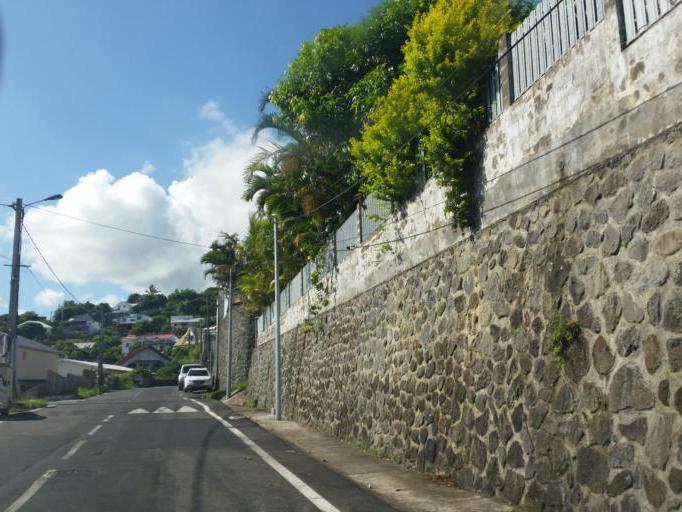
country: RE
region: Reunion
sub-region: Reunion
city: Sainte-Marie
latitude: -20.9190
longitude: 55.5172
